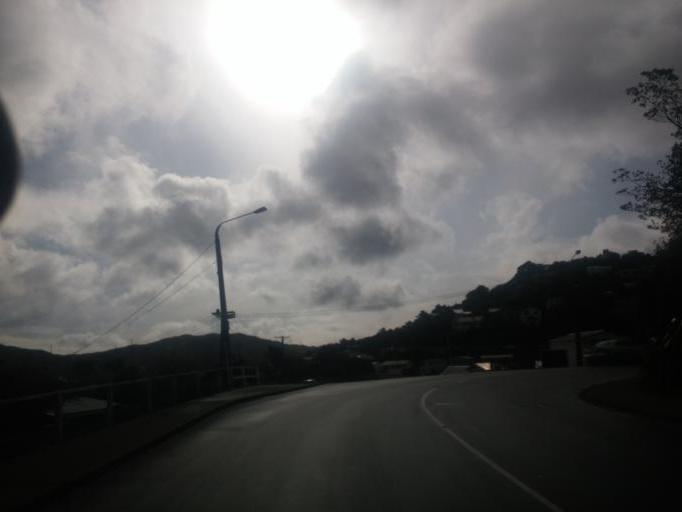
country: NZ
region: Wellington
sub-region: Wellington City
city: Kelburn
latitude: -41.2798
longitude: 174.7595
